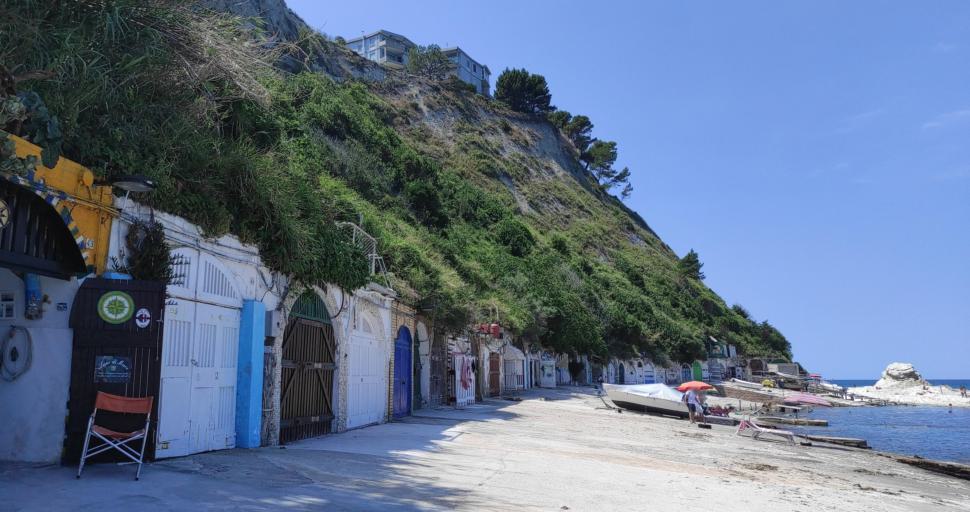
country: IT
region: The Marches
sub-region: Provincia di Ancona
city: Pietra la Croce
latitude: 43.6180
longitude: 13.5323
